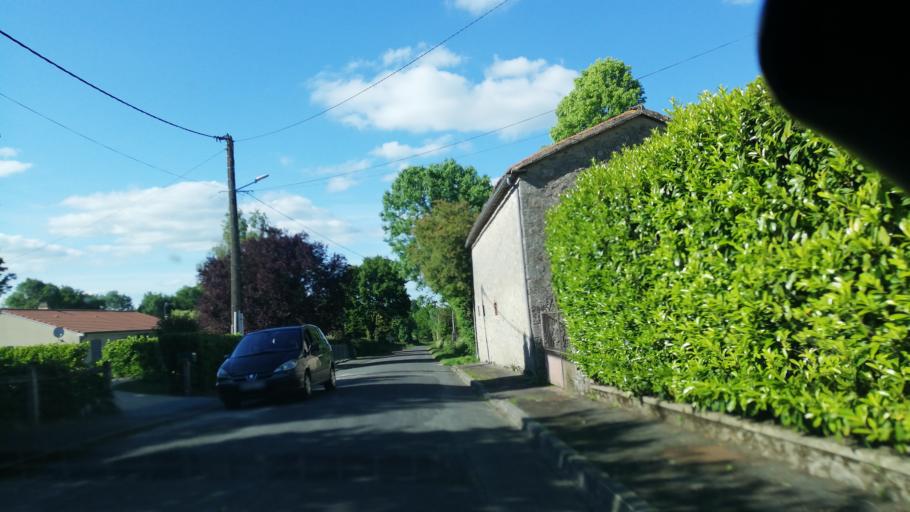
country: FR
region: Poitou-Charentes
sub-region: Departement des Deux-Sevres
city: Moncoutant
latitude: 46.6843
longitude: -0.5743
